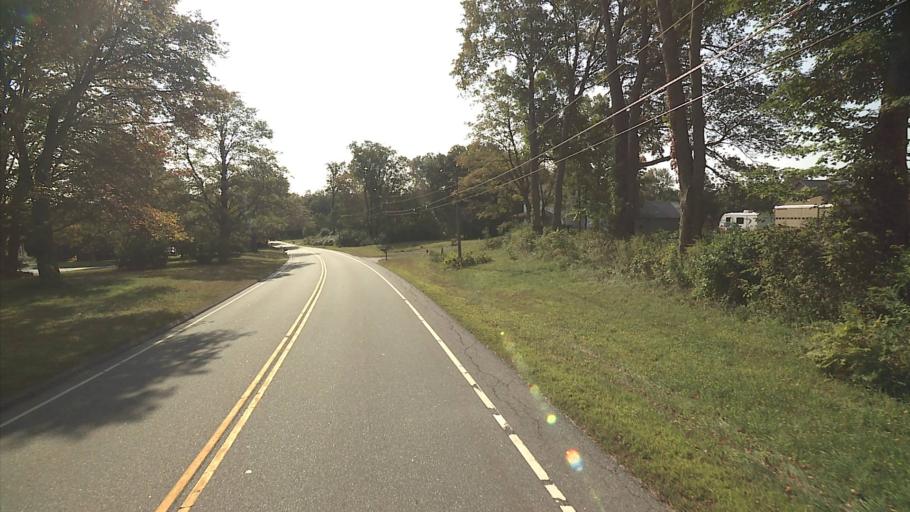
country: US
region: Connecticut
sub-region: Windham County
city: Willimantic
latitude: 41.6781
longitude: -72.2743
